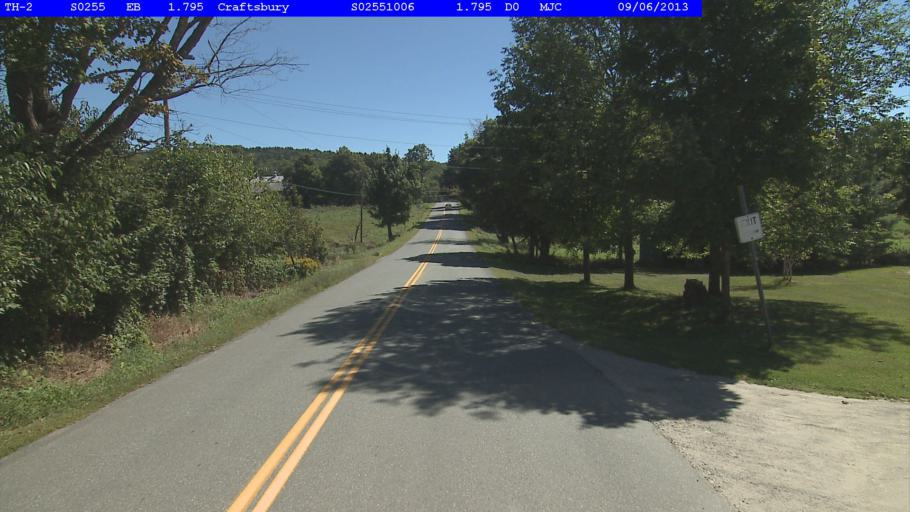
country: US
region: Vermont
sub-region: Caledonia County
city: Hardwick
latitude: 44.6411
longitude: -72.3413
